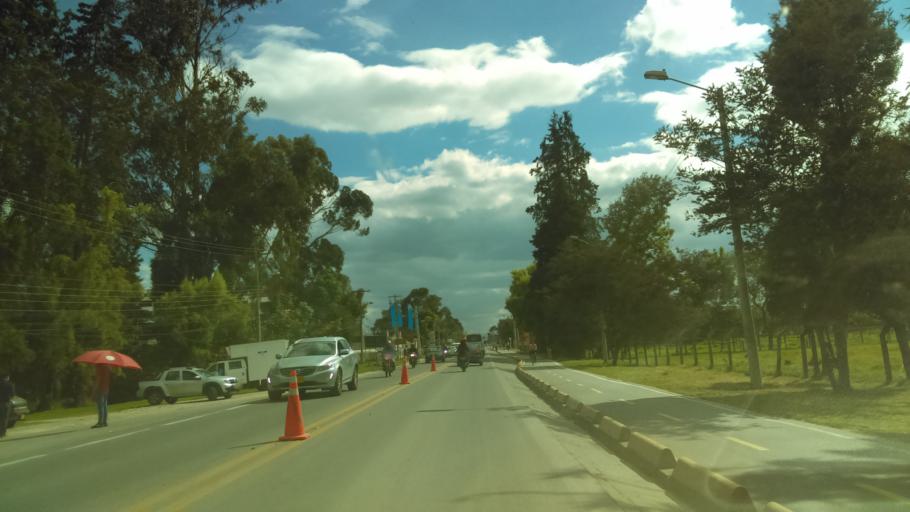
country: CO
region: Cundinamarca
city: Cajica
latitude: 4.9087
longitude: -74.0284
